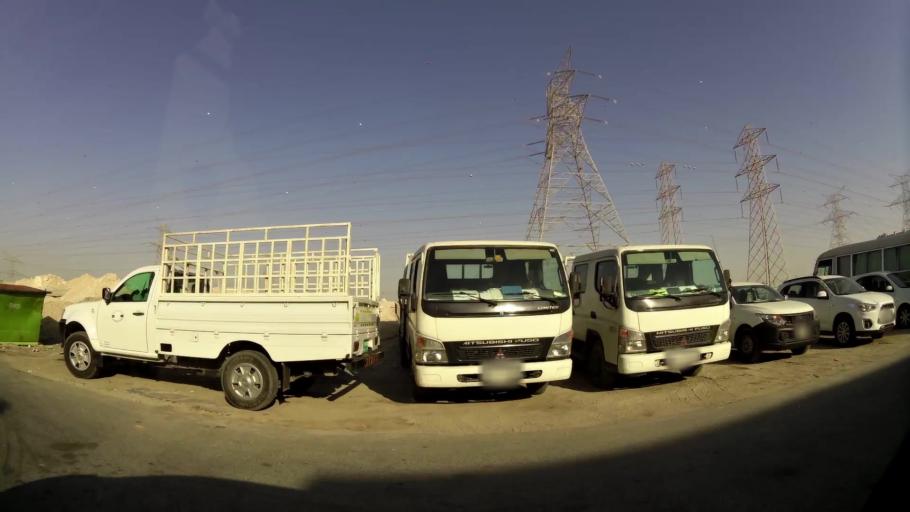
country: AE
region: Dubai
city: Dubai
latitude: 25.1345
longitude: 55.2566
